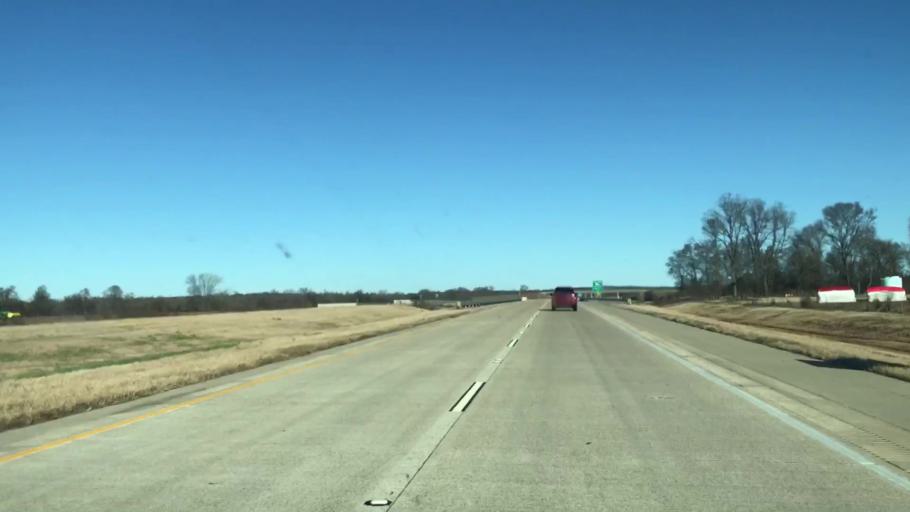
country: US
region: Louisiana
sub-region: Caddo Parish
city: Oil City
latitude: 32.7589
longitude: -93.8852
